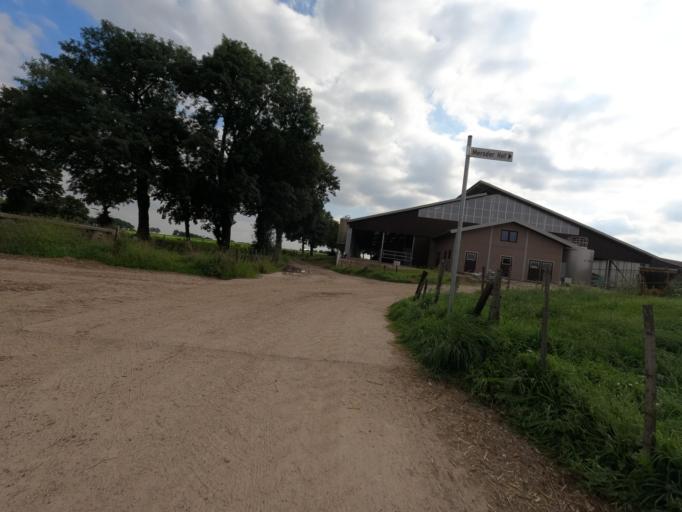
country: DE
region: North Rhine-Westphalia
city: Geilenkirchen
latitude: 50.9702
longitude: 6.1723
